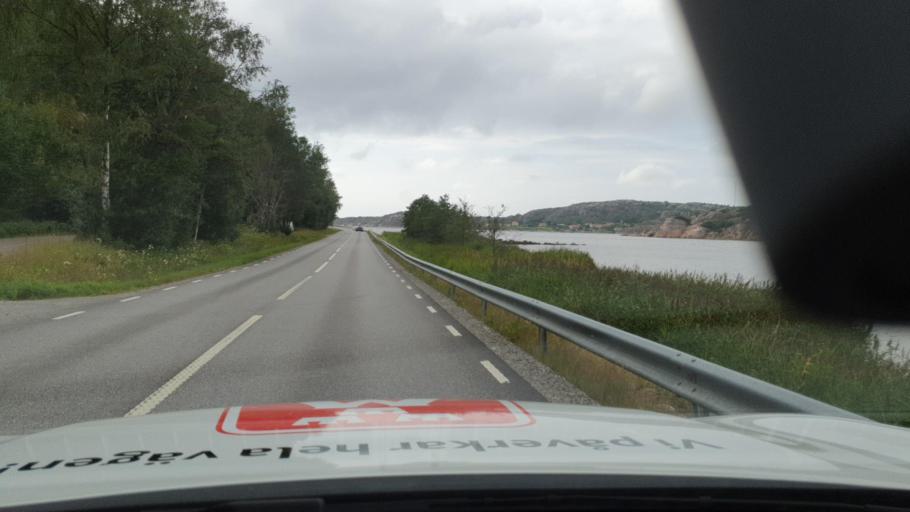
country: SE
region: Vaestra Goetaland
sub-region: Sotenas Kommun
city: Hunnebostrand
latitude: 58.4849
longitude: 11.3521
